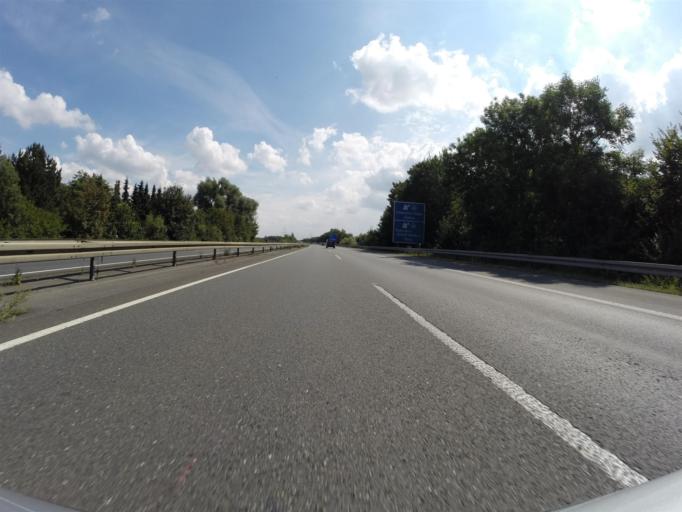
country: DE
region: North Rhine-Westphalia
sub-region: Regierungsbezirk Detmold
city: Paderborn
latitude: 51.7404
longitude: 8.7028
